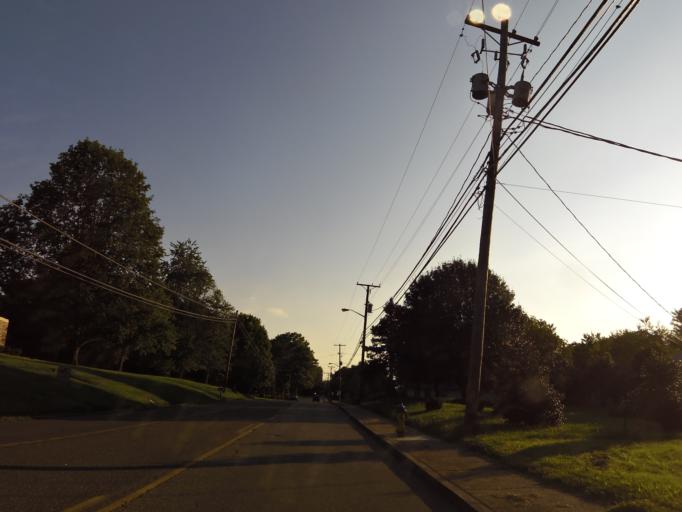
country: US
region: Tennessee
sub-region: Knox County
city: Knoxville
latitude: 35.9976
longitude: -83.9915
